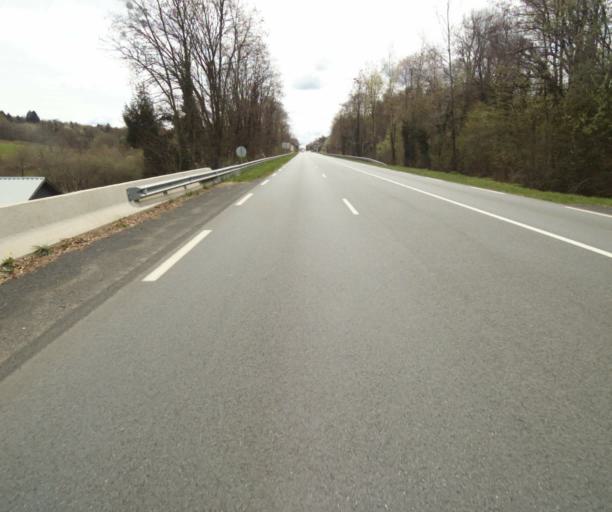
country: FR
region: Limousin
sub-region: Departement de la Correze
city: Sainte-Fortunade
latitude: 45.2049
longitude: 1.8281
